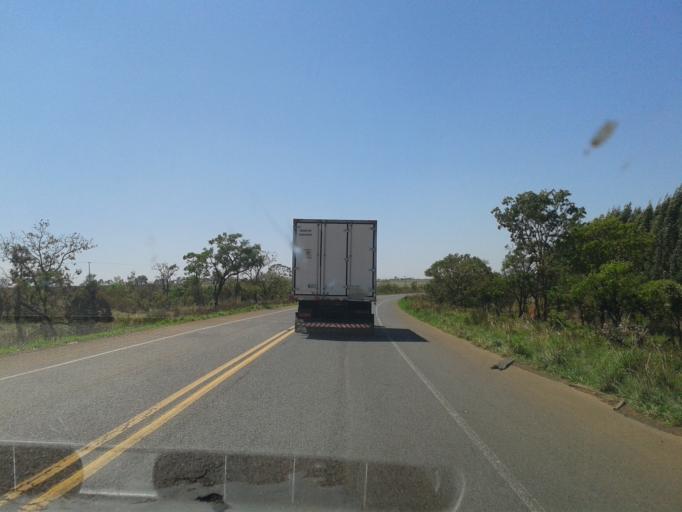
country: BR
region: Minas Gerais
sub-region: Patrocinio
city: Patrocinio
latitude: -19.2806
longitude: -47.4274
